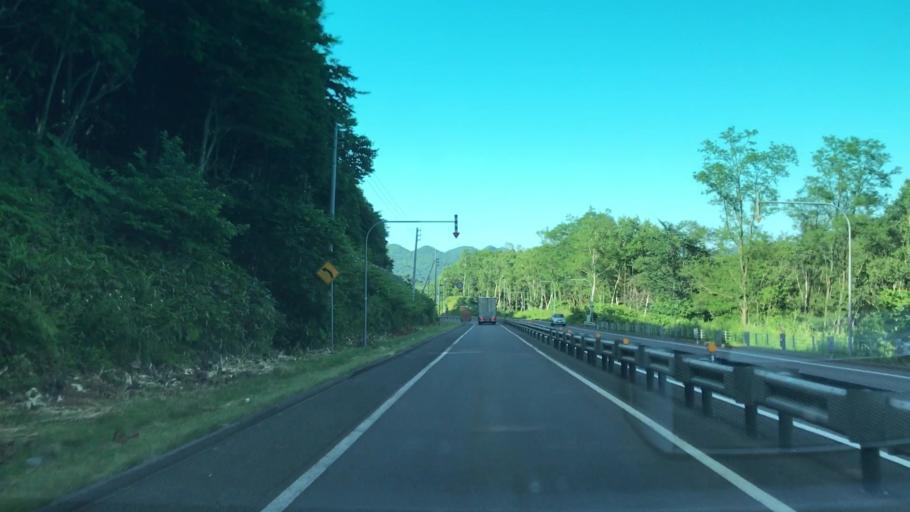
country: JP
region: Hokkaido
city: Yoichi
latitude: 43.0655
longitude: 140.6997
